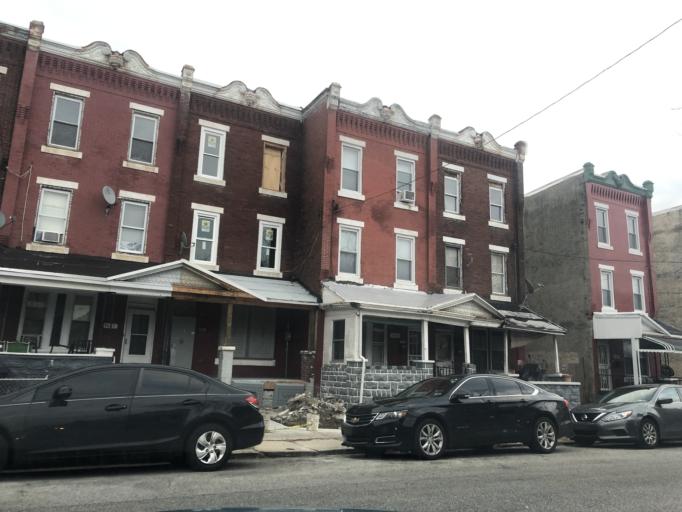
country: US
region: Pennsylvania
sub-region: Delaware County
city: Millbourne
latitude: 39.9778
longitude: -75.2340
